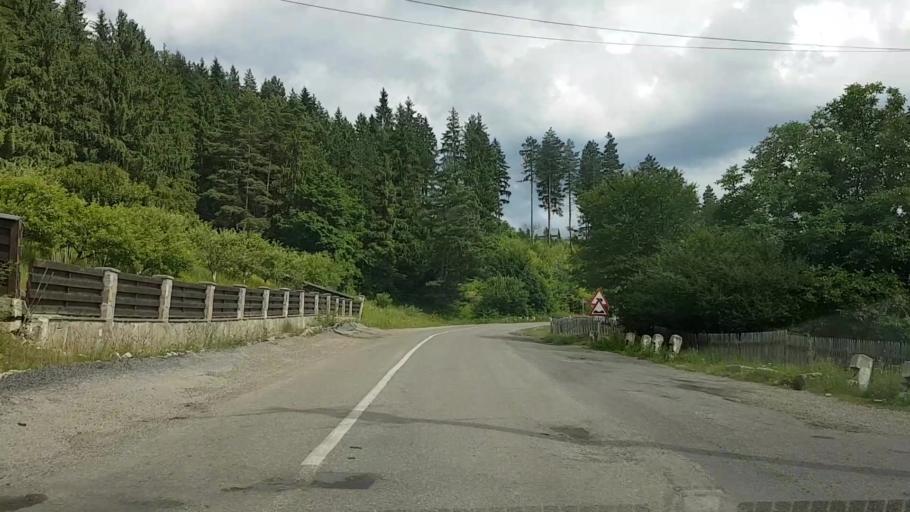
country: RO
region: Neamt
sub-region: Comuna Hangu
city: Hangu
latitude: 47.0093
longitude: 26.0890
